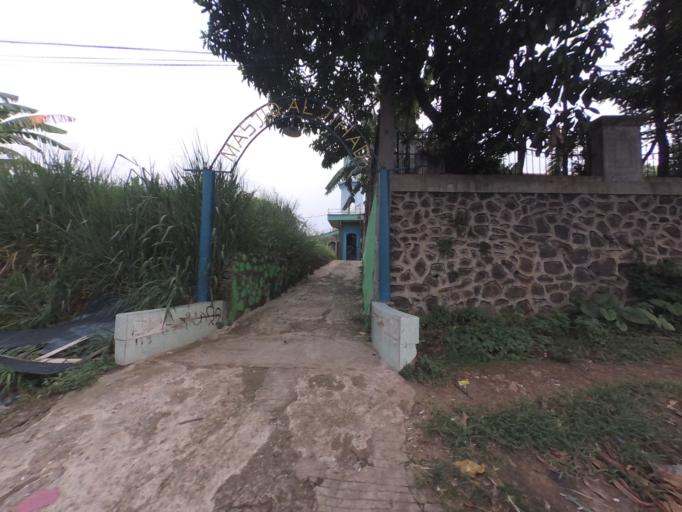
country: ID
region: West Java
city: Ciampea
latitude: -6.5628
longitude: 106.6833
